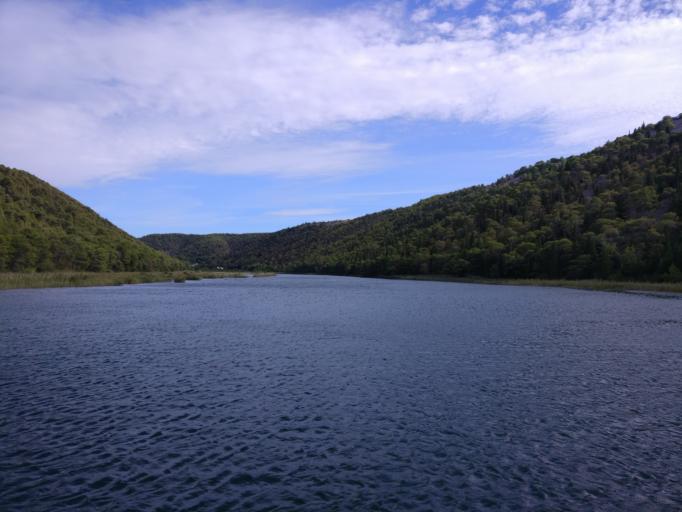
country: HR
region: Sibensko-Kniniska
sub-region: Grad Sibenik
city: Sibenik
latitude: 43.8178
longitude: 15.9494
